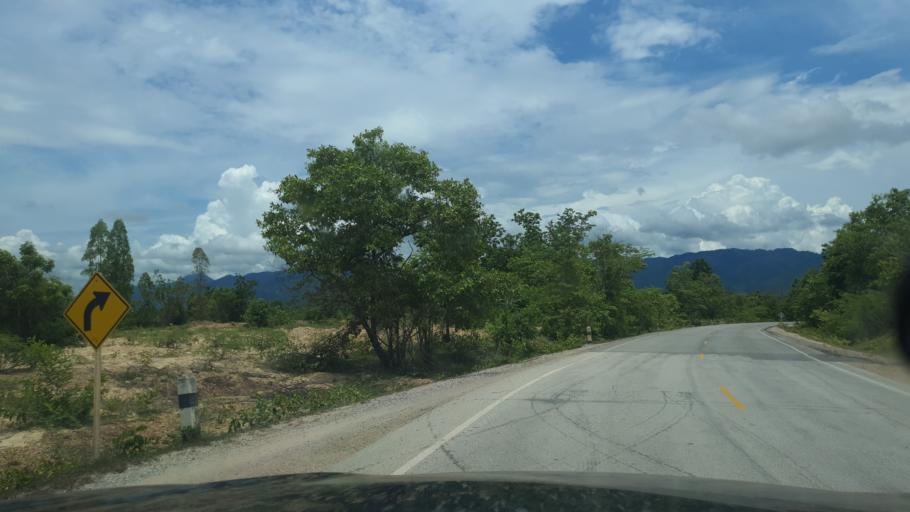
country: TH
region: Lampang
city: Sop Prap
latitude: 17.9331
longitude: 99.3683
